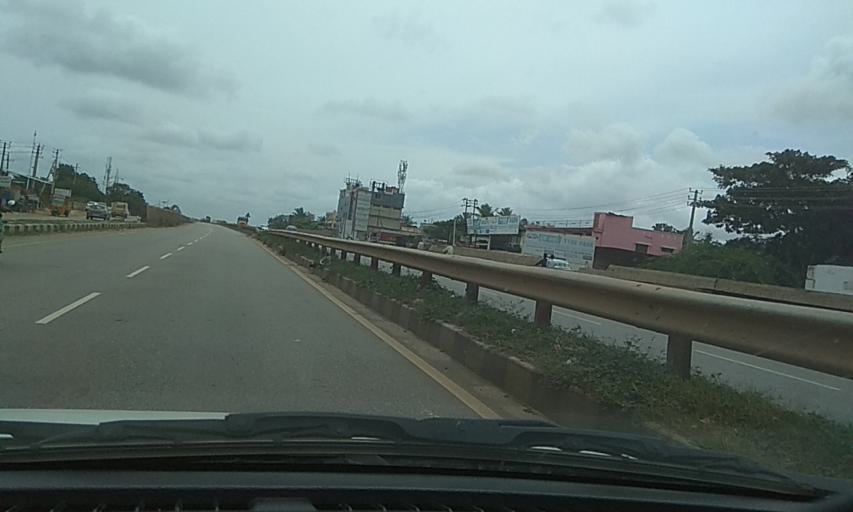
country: IN
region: Karnataka
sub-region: Chitradurga
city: Chitradurga
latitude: 14.2358
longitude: 76.3999
